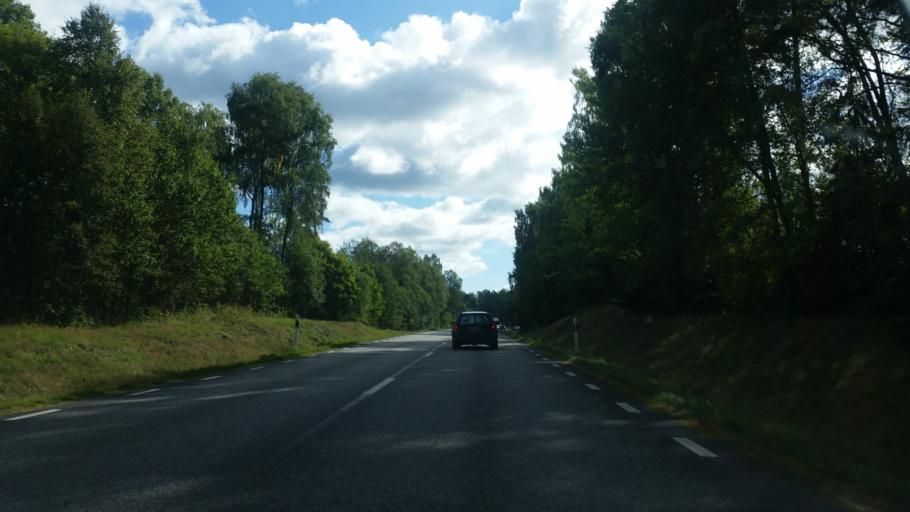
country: SE
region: Joenkoeping
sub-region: Varnamo Kommun
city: Forsheda
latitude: 57.1671
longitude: 13.8307
